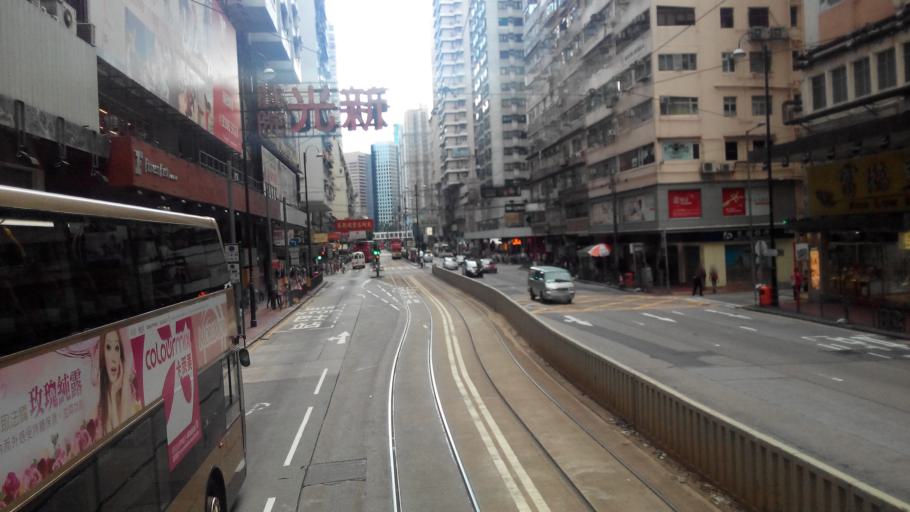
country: HK
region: Wanchai
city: Wan Chai
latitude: 22.2909
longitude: 114.1990
